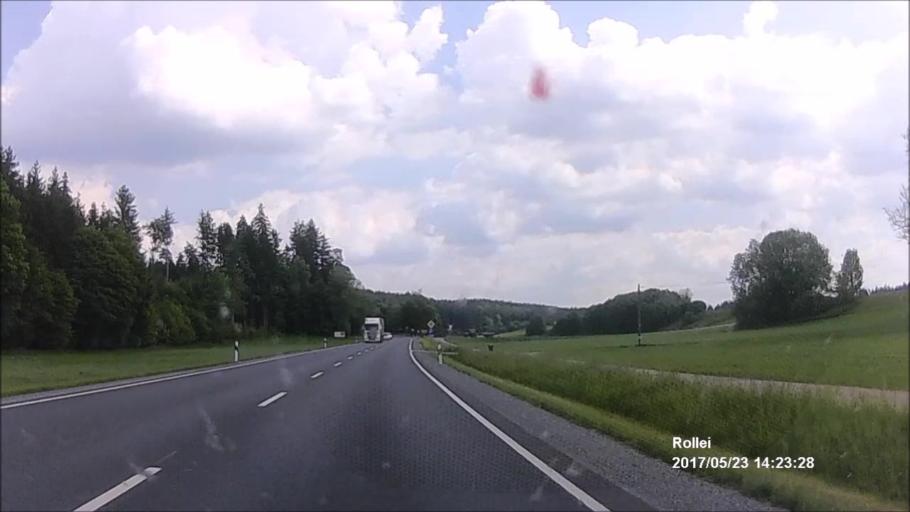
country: DE
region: Bavaria
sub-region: Upper Bavaria
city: Babensham
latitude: 48.0445
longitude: 12.2920
